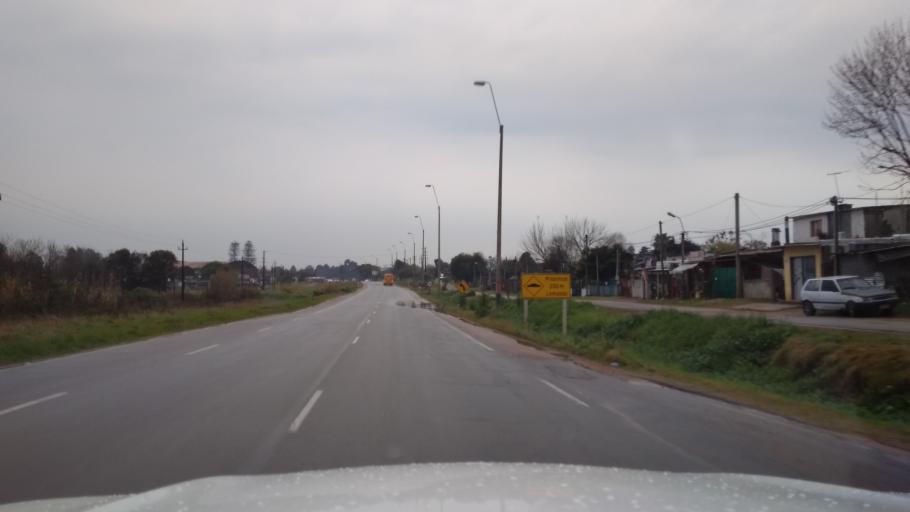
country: UY
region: Canelones
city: Toledo
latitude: -34.7576
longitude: -56.1125
